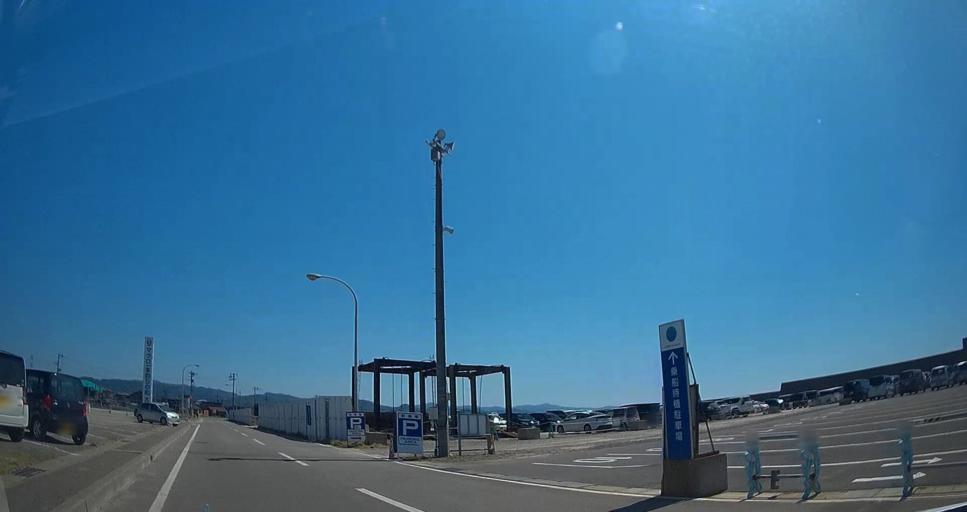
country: JP
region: Hokkaido
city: Hakodate
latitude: 41.5250
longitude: 140.8995
